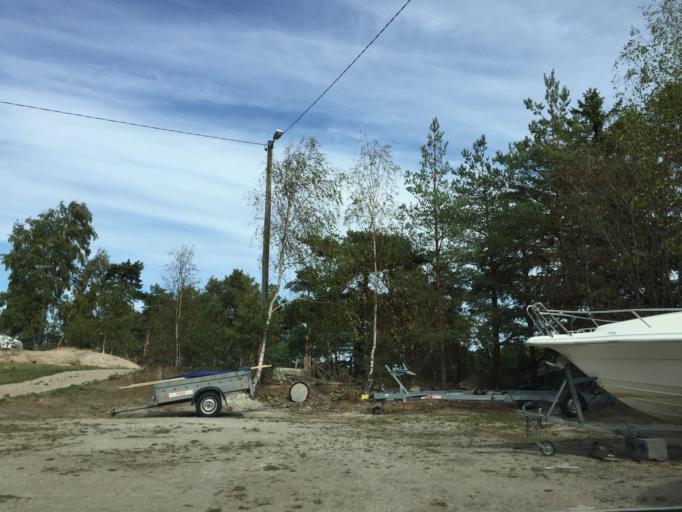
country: NO
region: Ostfold
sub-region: Fredrikstad
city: Fredrikstad
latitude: 59.1017
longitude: 10.9342
